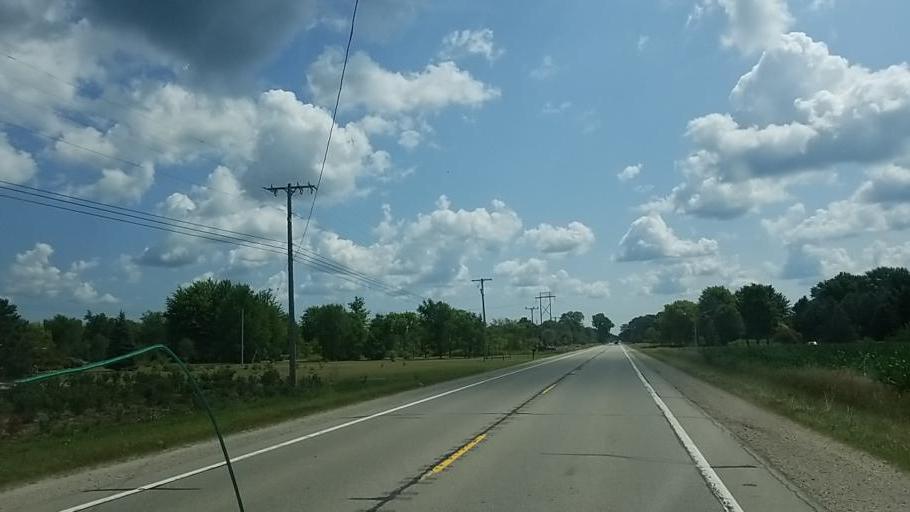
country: US
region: Michigan
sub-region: Muskegon County
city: Ravenna
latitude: 43.2350
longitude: -85.9866
